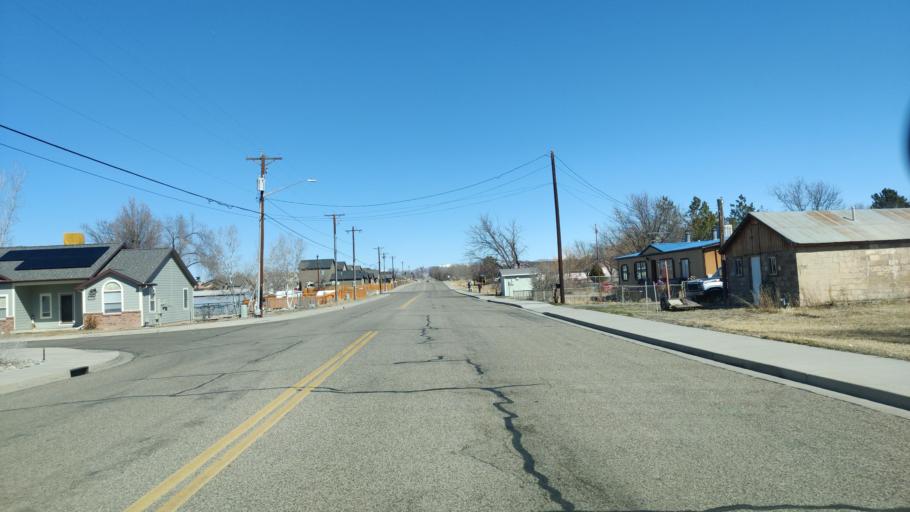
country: US
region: Colorado
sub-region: Mesa County
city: Fruita
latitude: 39.1719
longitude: -108.7197
